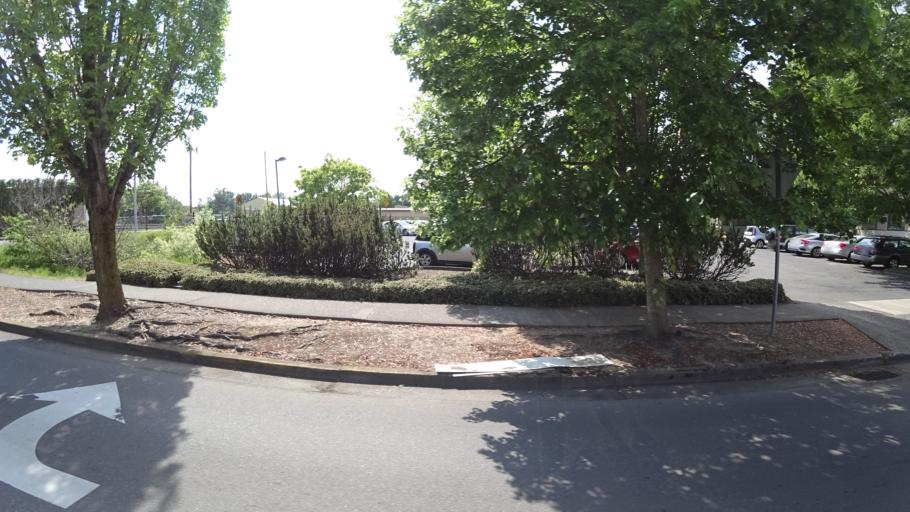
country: US
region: Oregon
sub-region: Washington County
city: Beaverton
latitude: 45.4826
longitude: -122.7945
